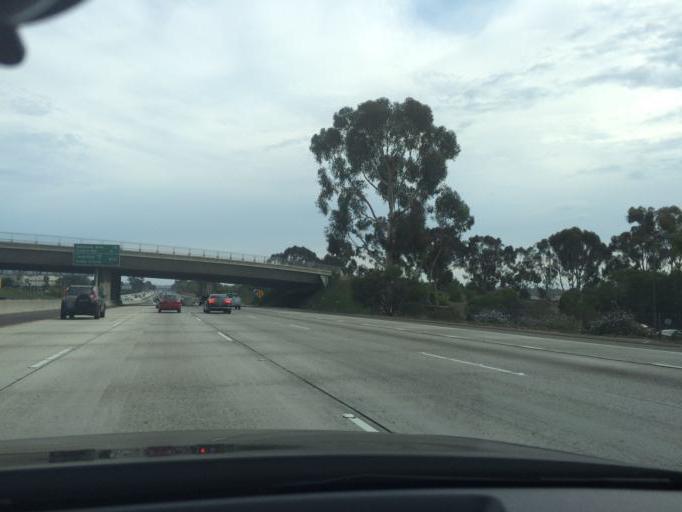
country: US
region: California
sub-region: San Diego County
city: San Diego
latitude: 32.8038
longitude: -117.1542
